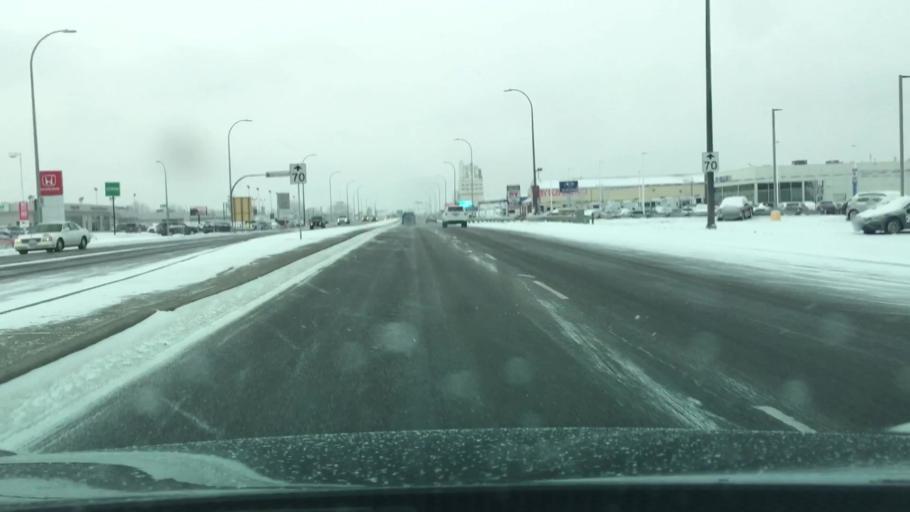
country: CA
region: Alberta
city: Lethbridge
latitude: 49.6983
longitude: -112.7889
